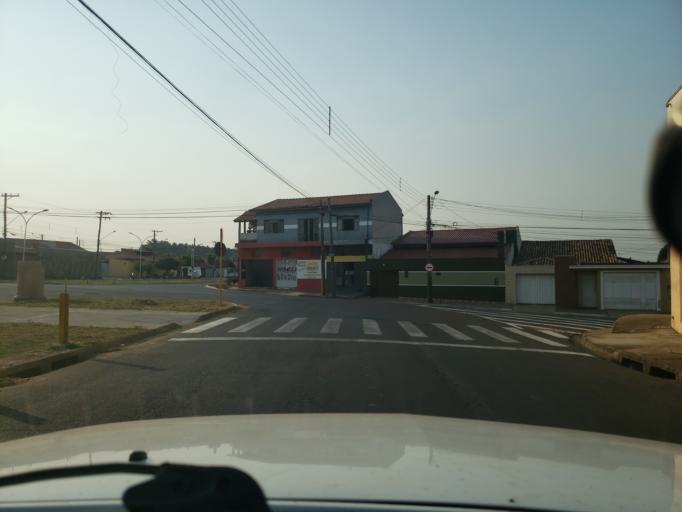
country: BR
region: Sao Paulo
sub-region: Moji-Guacu
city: Mogi-Gaucu
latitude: -22.3315
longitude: -46.9479
